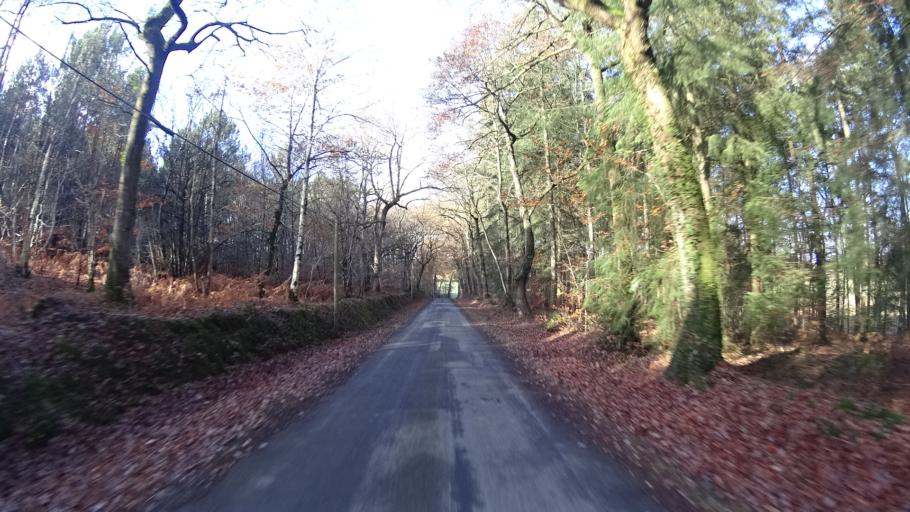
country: FR
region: Brittany
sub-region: Departement d'Ille-et-Vilaine
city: Sixt-sur-Aff
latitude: 47.8285
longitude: -2.0744
